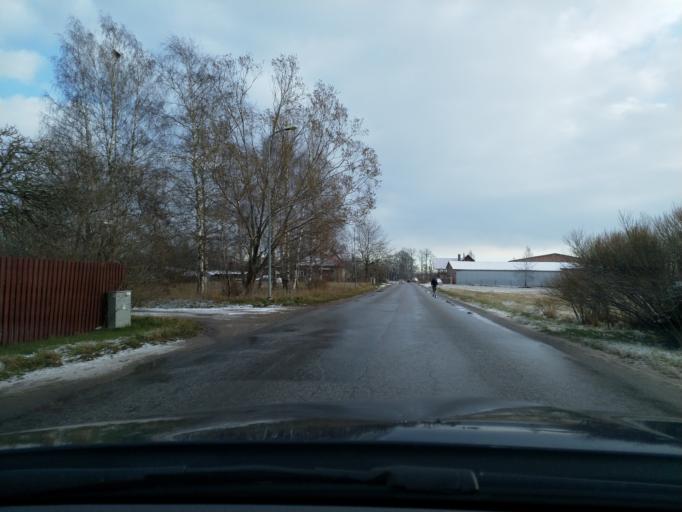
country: LV
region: Kuldigas Rajons
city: Kuldiga
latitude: 56.9601
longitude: 21.9884
